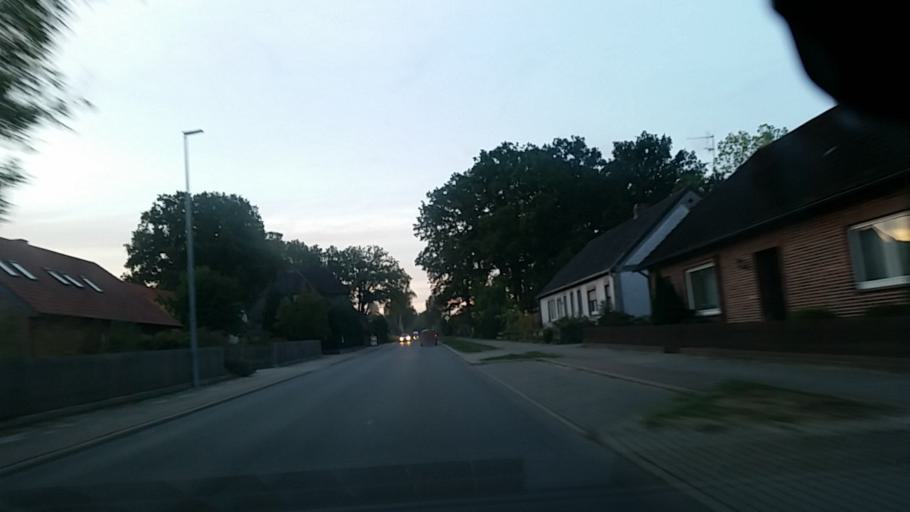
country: DE
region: Lower Saxony
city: Wieren
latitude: 52.8831
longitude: 10.6618
